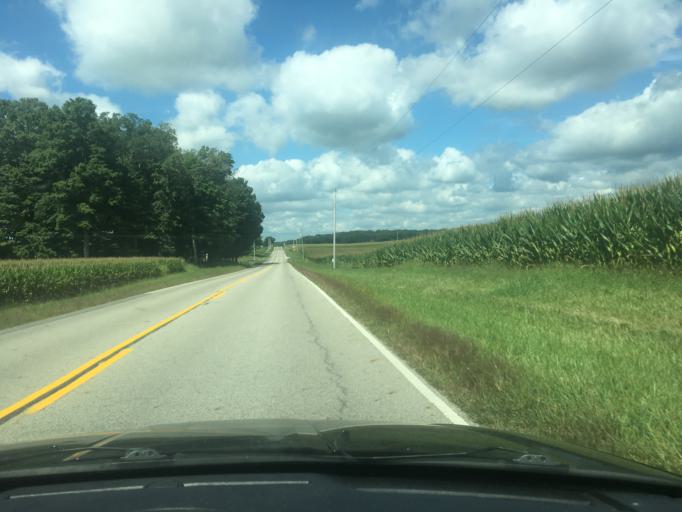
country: US
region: Ohio
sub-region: Logan County
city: West Liberty
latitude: 40.2361
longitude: -83.7103
